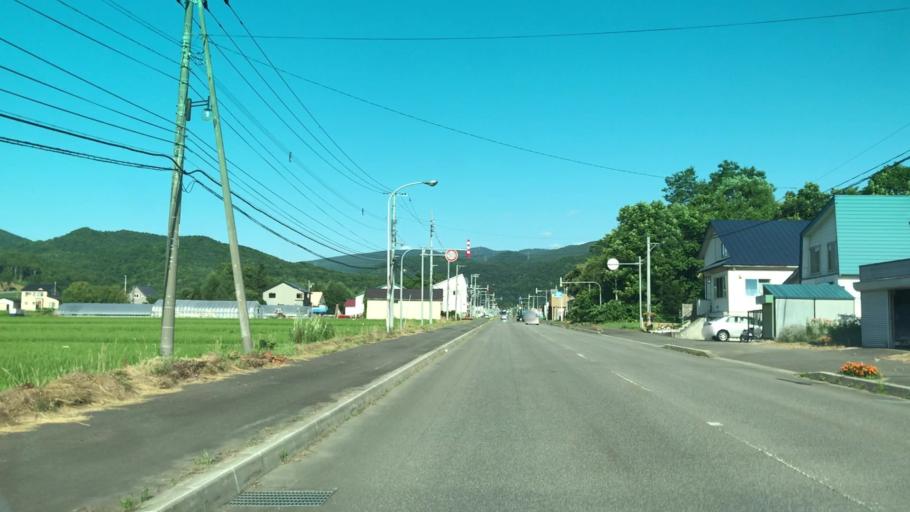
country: JP
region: Hokkaido
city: Yoichi
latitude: 43.0509
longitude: 140.8278
